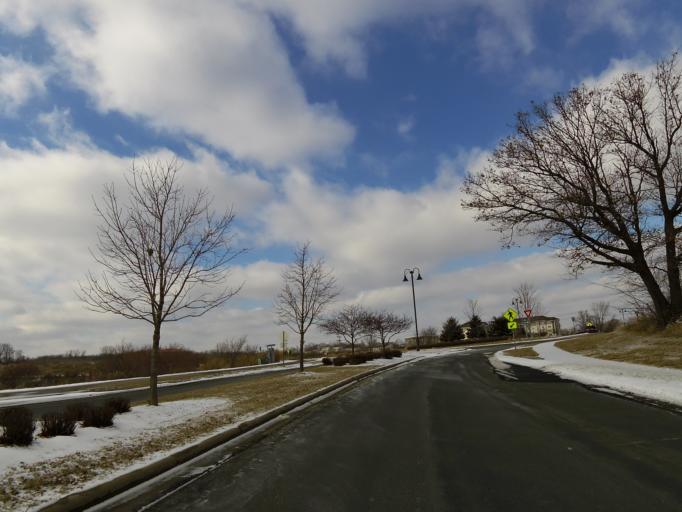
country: US
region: Minnesota
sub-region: Scott County
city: Prior Lake
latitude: 44.7453
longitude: -93.4444
